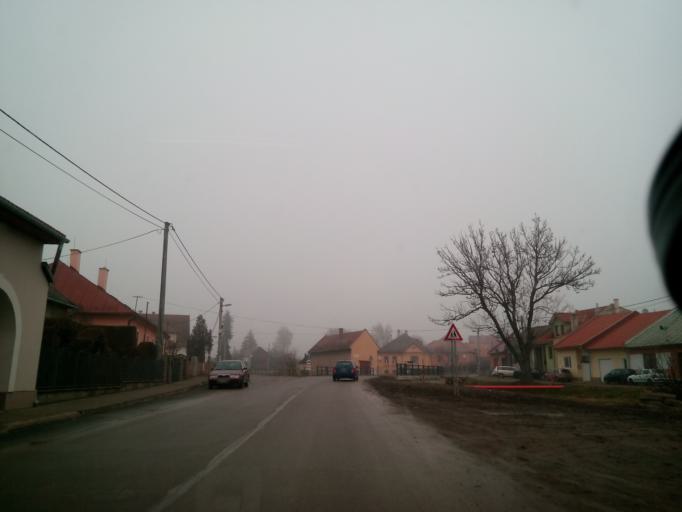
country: SK
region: Presovsky
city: Spisske Podhradie
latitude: 49.0031
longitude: 20.7568
